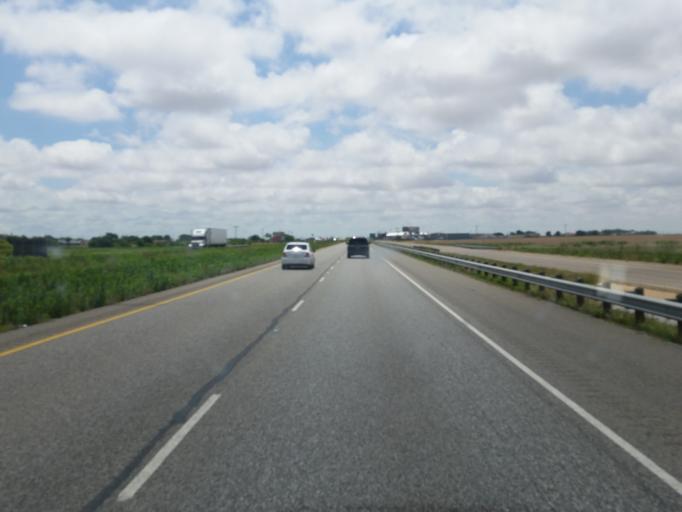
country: US
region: Texas
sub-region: Lubbock County
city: Slaton
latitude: 33.4270
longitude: -101.6552
